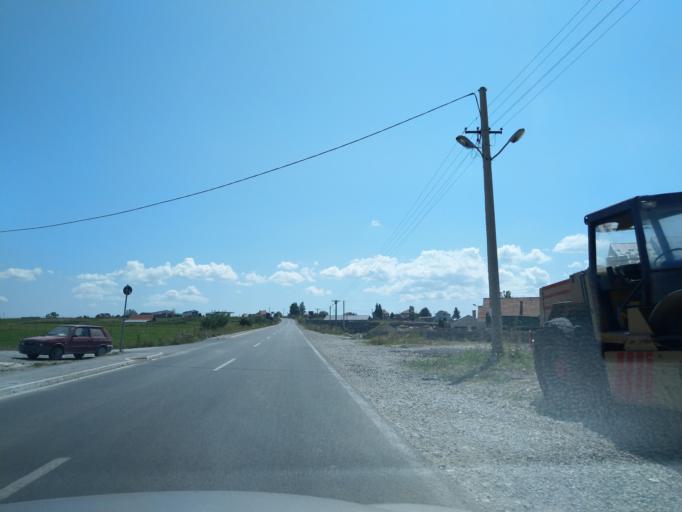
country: RS
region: Central Serbia
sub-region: Zlatiborski Okrug
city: Sjenica
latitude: 43.2777
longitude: 19.9834
